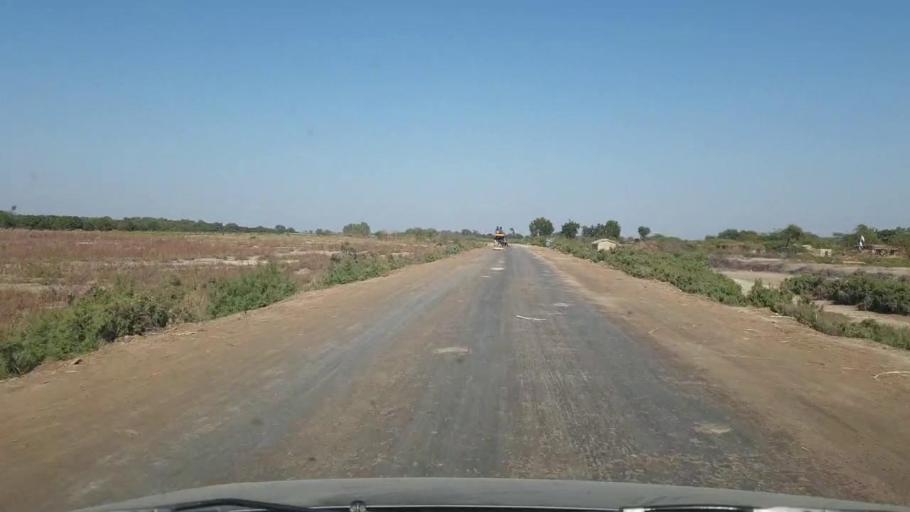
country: PK
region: Sindh
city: Samaro
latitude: 25.3310
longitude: 69.3061
